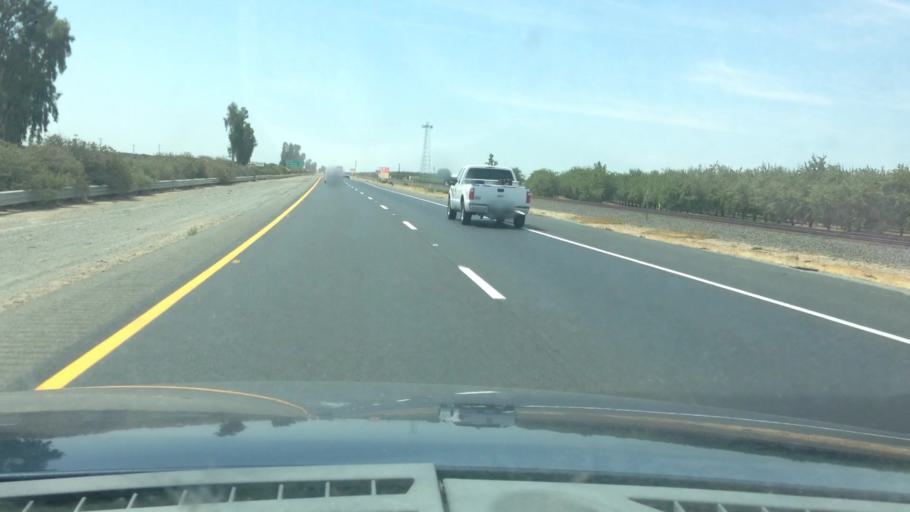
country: US
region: California
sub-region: Tulare County
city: Earlimart
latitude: 35.8685
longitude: -119.2706
